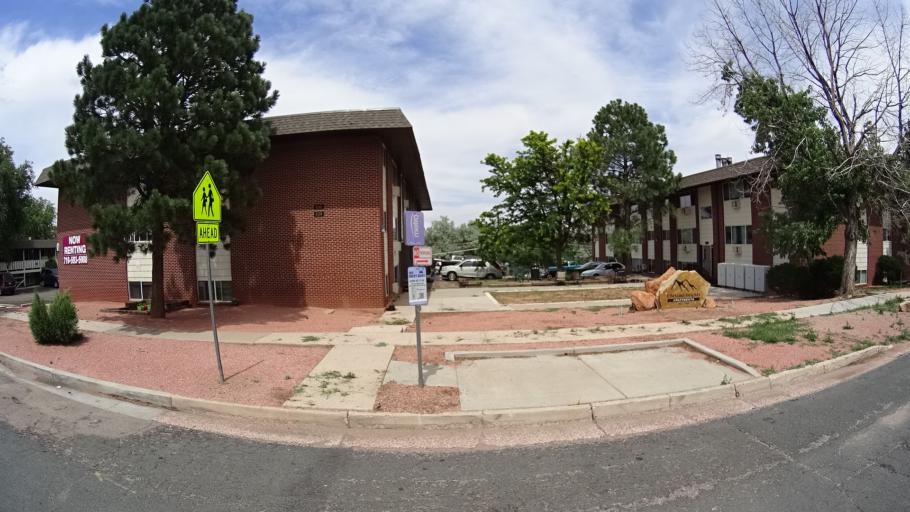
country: US
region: Colorado
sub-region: El Paso County
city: Colorado Springs
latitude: 38.8926
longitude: -104.8347
